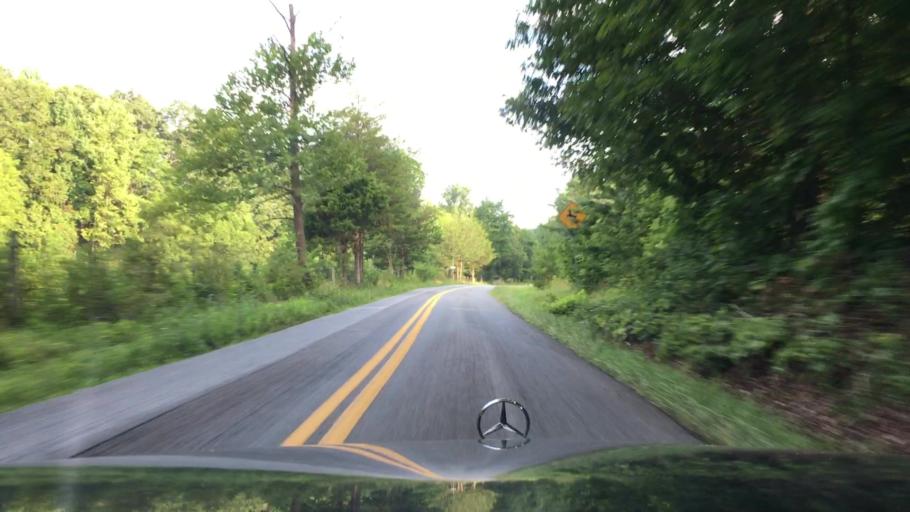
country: US
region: Virginia
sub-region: Campbell County
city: Timberlake
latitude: 37.2786
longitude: -79.2690
